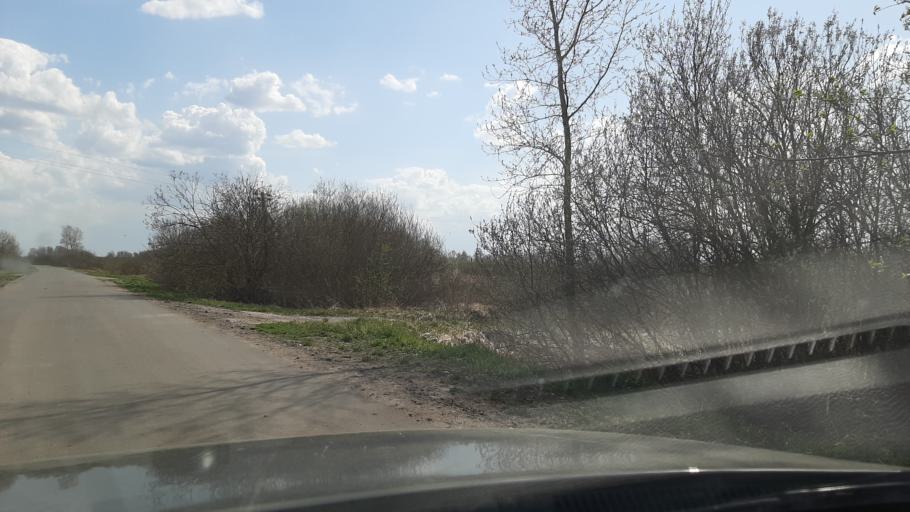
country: RU
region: Ivanovo
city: Privolzhsk
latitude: 57.3290
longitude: 41.2353
